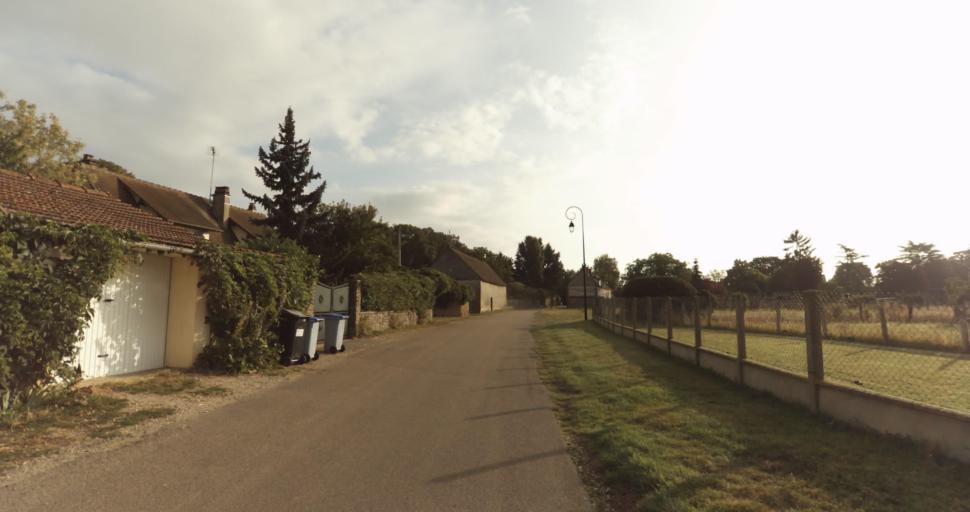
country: FR
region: Centre
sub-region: Departement d'Eure-et-Loir
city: Vert-en-Drouais
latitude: 48.7820
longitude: 1.3148
